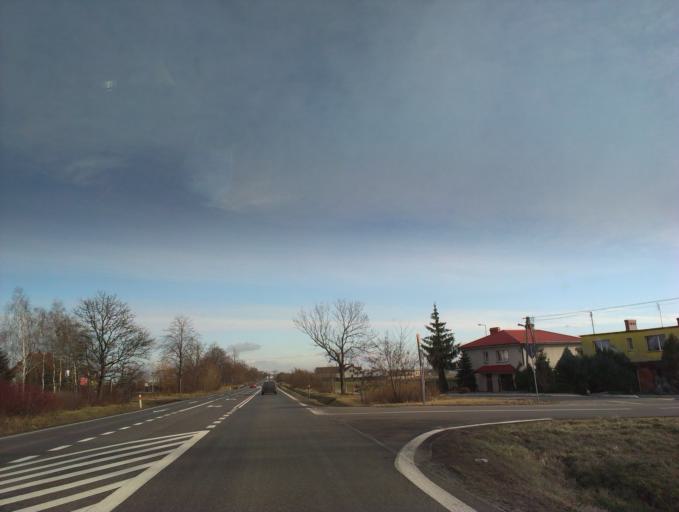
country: PL
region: Kujawsko-Pomorskie
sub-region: Powiat torunski
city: Obrowo
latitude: 52.9702
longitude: 18.8877
